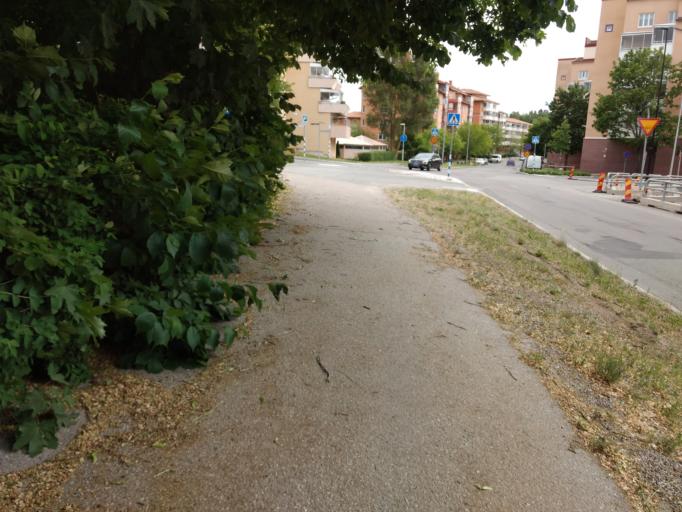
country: SE
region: Stockholm
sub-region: Upplands Vasby Kommun
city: Upplands Vaesby
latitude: 59.5232
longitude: 17.9044
